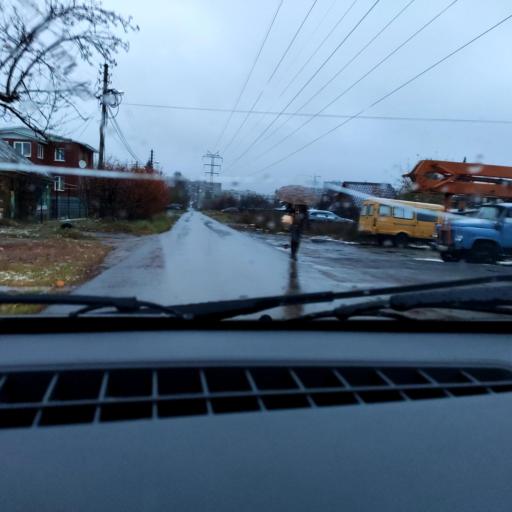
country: RU
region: Bashkortostan
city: Avdon
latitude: 54.6903
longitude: 55.8114
